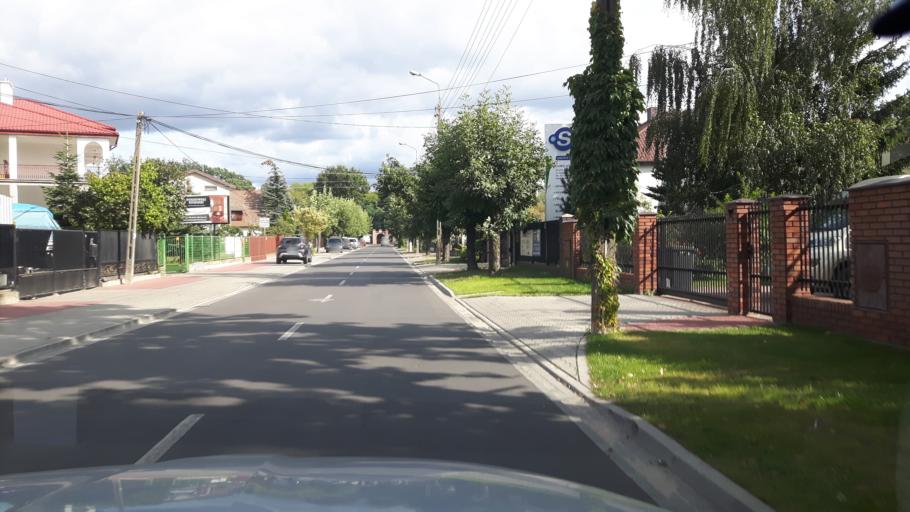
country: PL
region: Masovian Voivodeship
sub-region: Powiat wolominski
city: Kobylka
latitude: 52.3379
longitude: 21.2005
